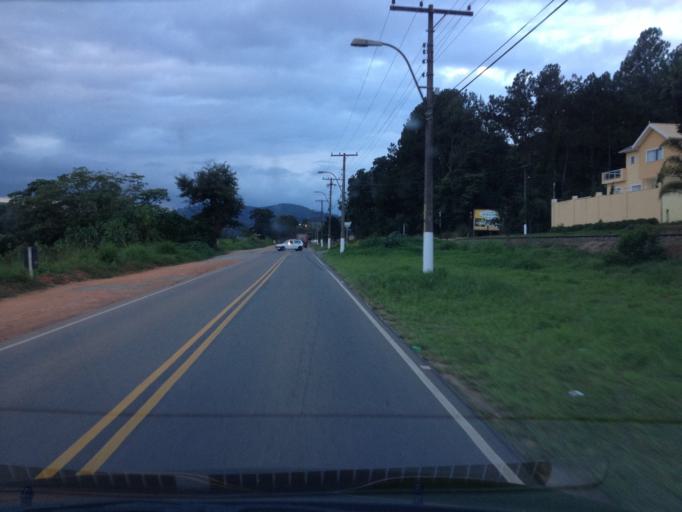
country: BR
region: Minas Gerais
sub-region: Sao Lourenco
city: Sao Lourenco
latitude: -22.0949
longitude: -45.0455
